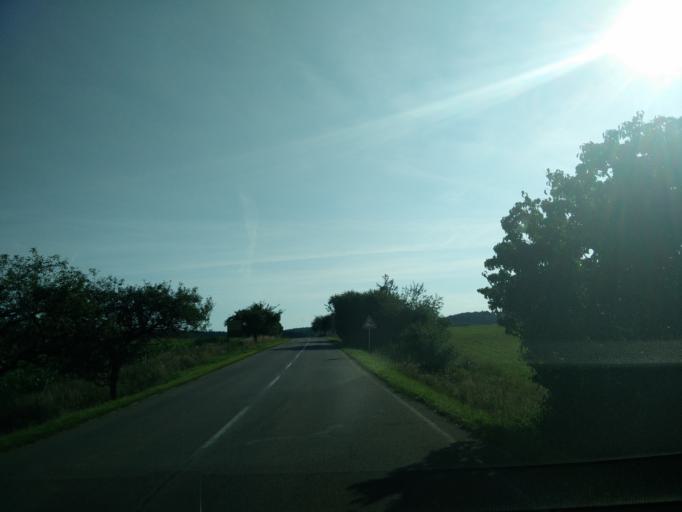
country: SK
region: Nitriansky
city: Handlova
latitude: 48.8801
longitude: 18.7443
